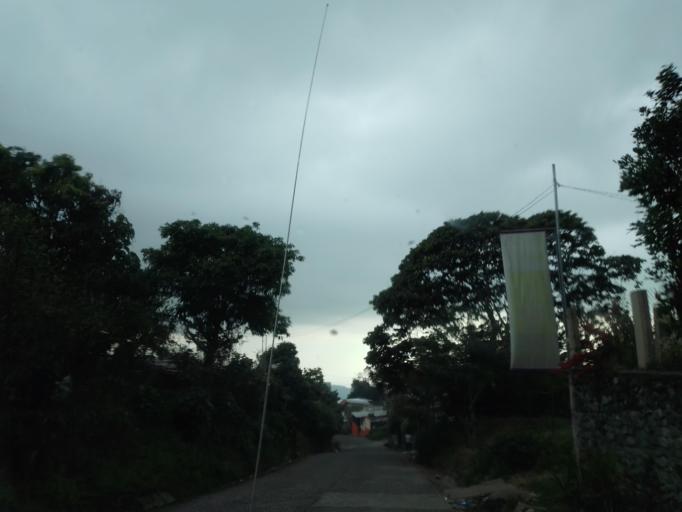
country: MX
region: Chiapas
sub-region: Union Juarez
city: Santo Domingo
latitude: 15.0656
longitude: -92.0812
